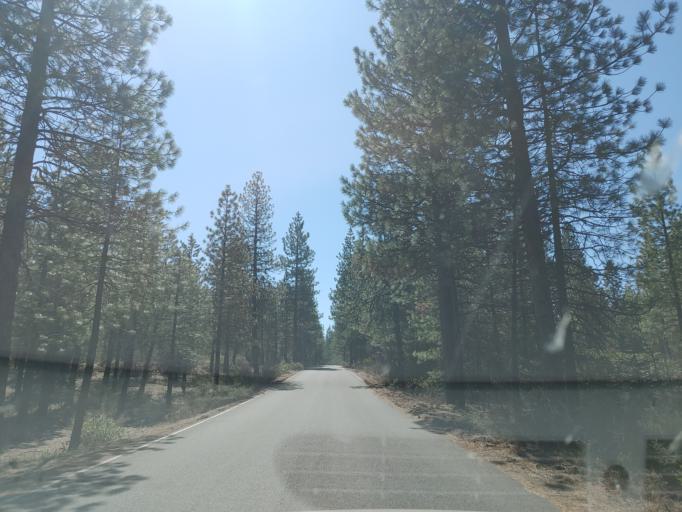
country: US
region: California
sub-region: Siskiyou County
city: McCloud
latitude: 41.2401
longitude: -122.0063
